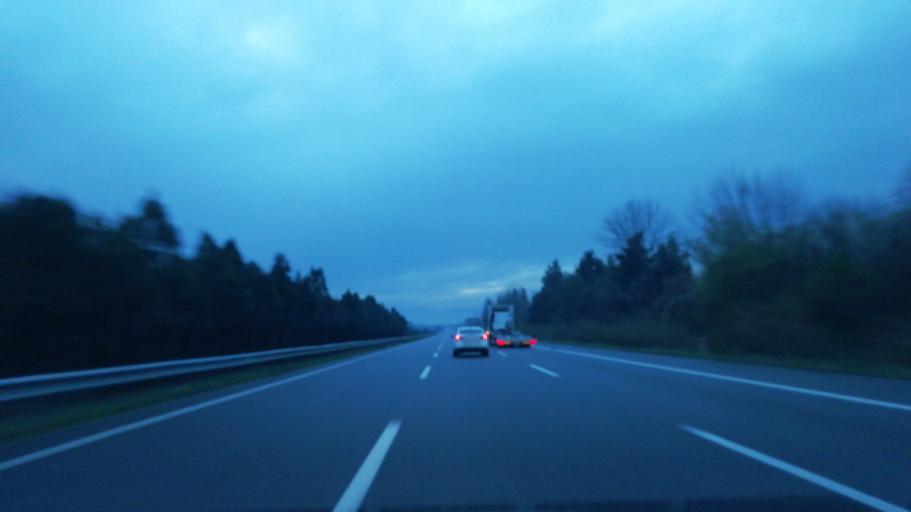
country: TR
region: Duzce
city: Cilimli
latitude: 40.8231
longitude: 31.0637
